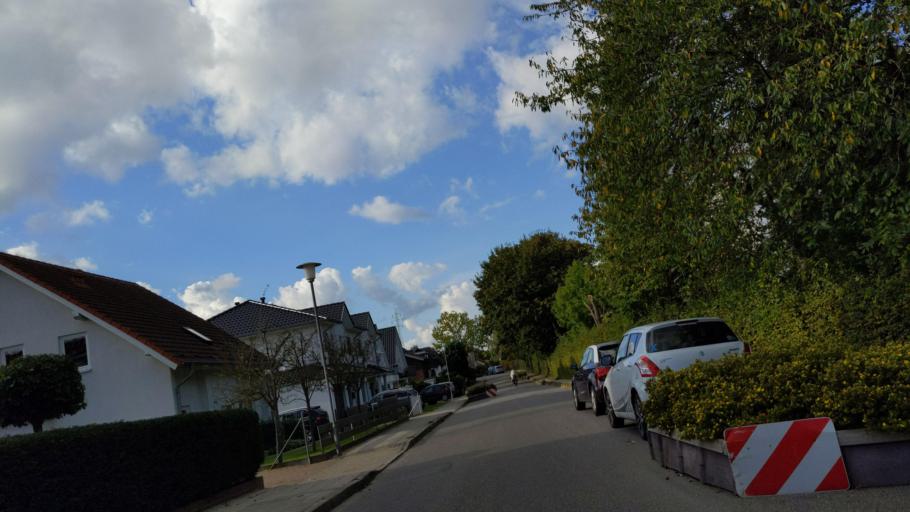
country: DE
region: Schleswig-Holstein
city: Scharbeutz
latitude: 54.0207
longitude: 10.7427
